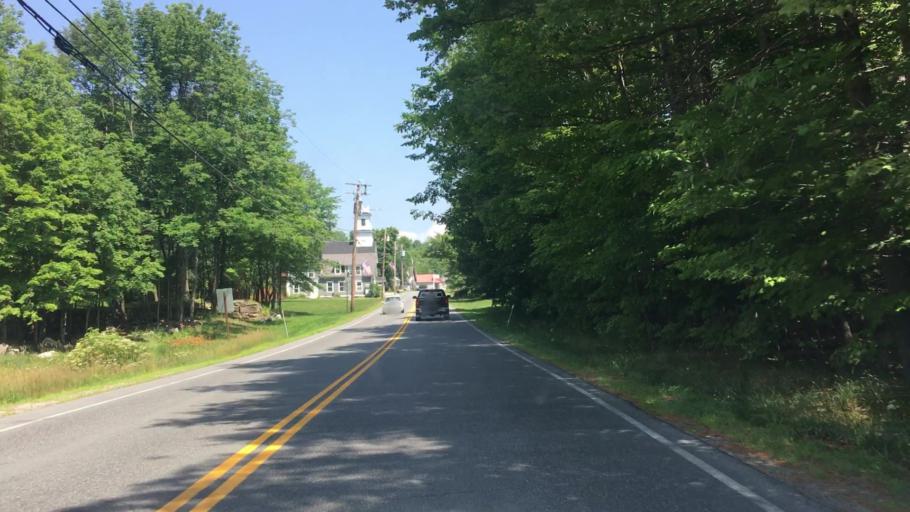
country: US
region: New Hampshire
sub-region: Sullivan County
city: Grantham
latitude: 43.4867
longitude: -72.1368
